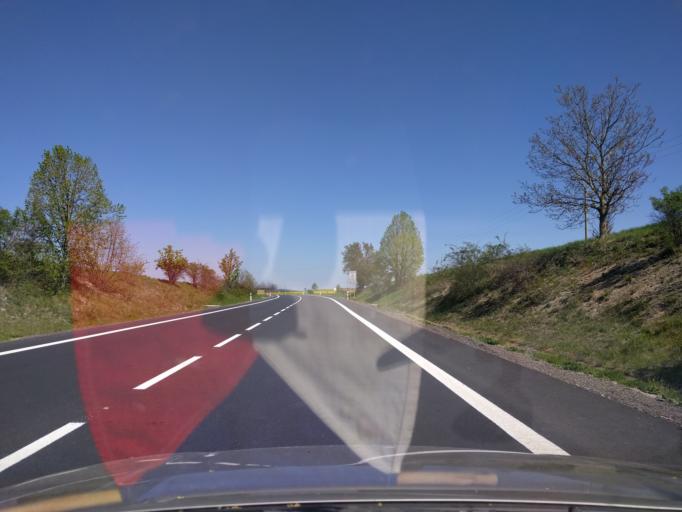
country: CZ
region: Central Bohemia
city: Prerov nad Labem
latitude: 50.1319
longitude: 14.8462
